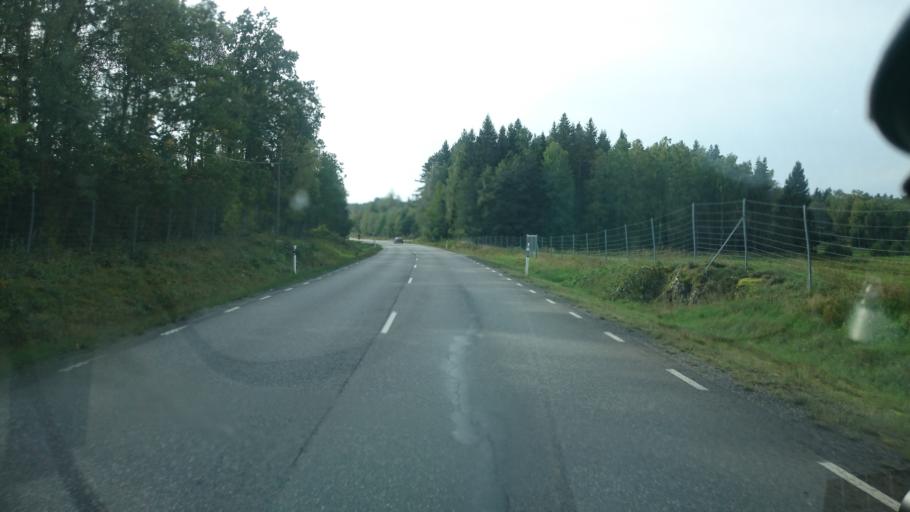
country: SE
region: Vaestra Goetaland
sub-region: Alingsas Kommun
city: Alingsas
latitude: 58.0083
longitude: 12.4451
